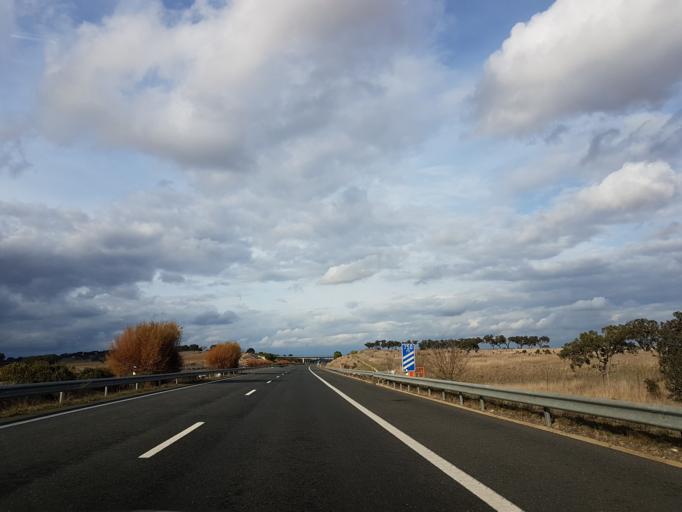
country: PT
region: Beja
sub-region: Aljustrel
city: Aljustrel
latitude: 37.8811
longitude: -8.2375
